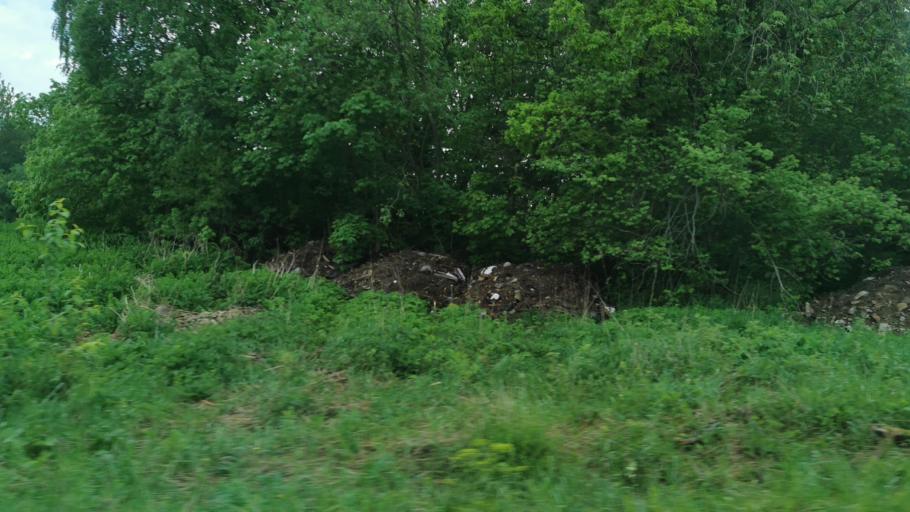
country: EE
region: Laeaene-Virumaa
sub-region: Vinni vald
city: Vinni
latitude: 59.2683
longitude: 26.3596
